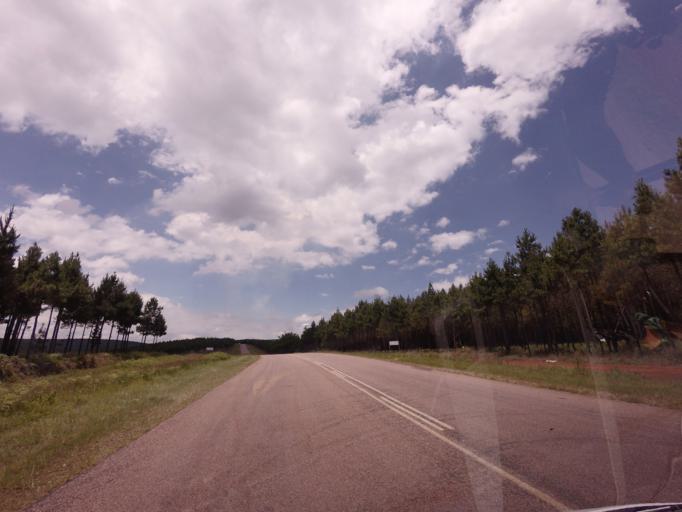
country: ZA
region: Mpumalanga
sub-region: Ehlanzeni District
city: Graksop
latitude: -25.0645
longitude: 30.8123
